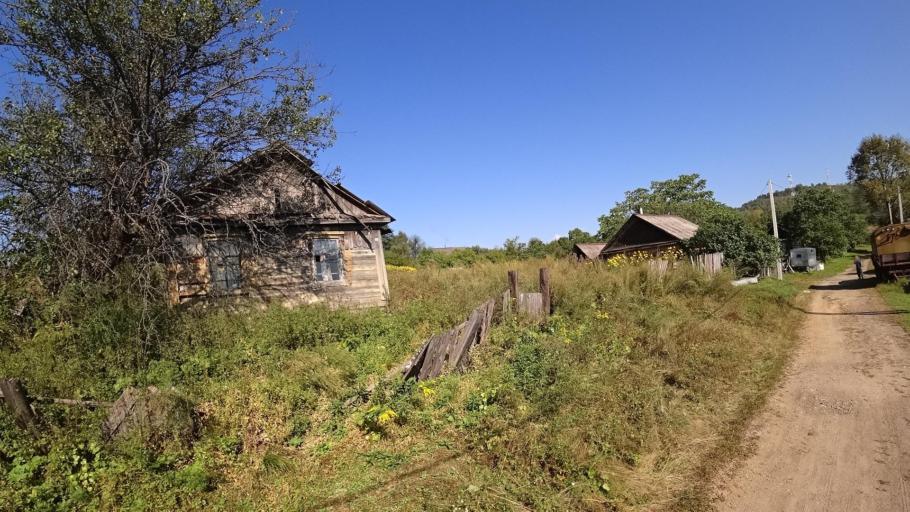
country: RU
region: Jewish Autonomous Oblast
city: Bira
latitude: 49.0045
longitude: 132.4611
